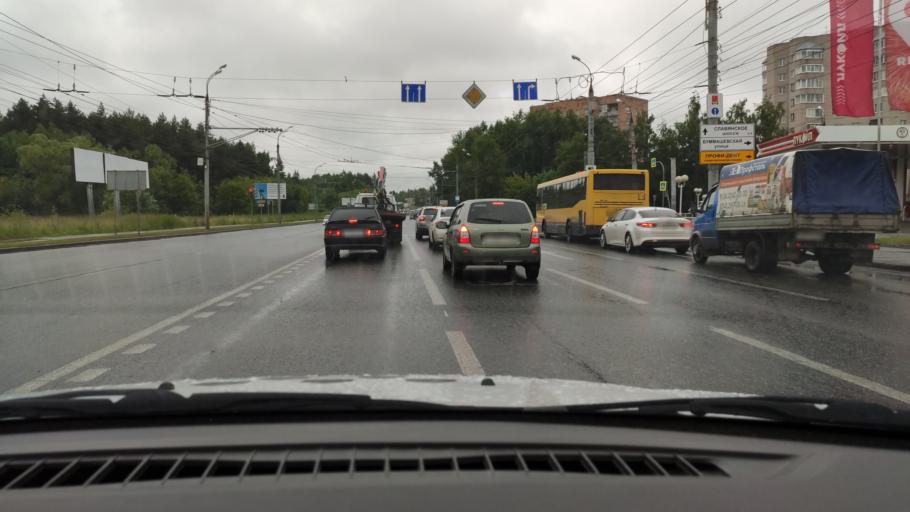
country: RU
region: Udmurtiya
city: Izhevsk
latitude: 56.8827
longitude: 53.2260
